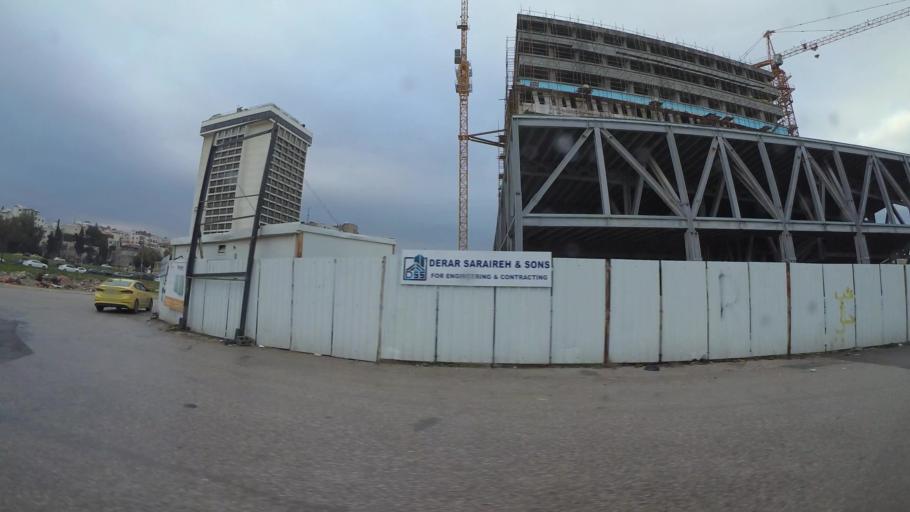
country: JO
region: Amman
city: Amman
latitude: 31.9761
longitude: 35.9084
